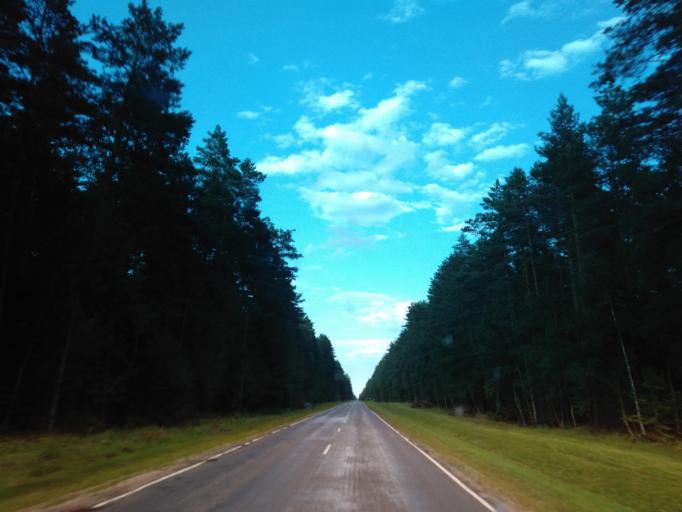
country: BY
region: Minsk
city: Uzda
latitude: 53.4234
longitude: 27.4346
